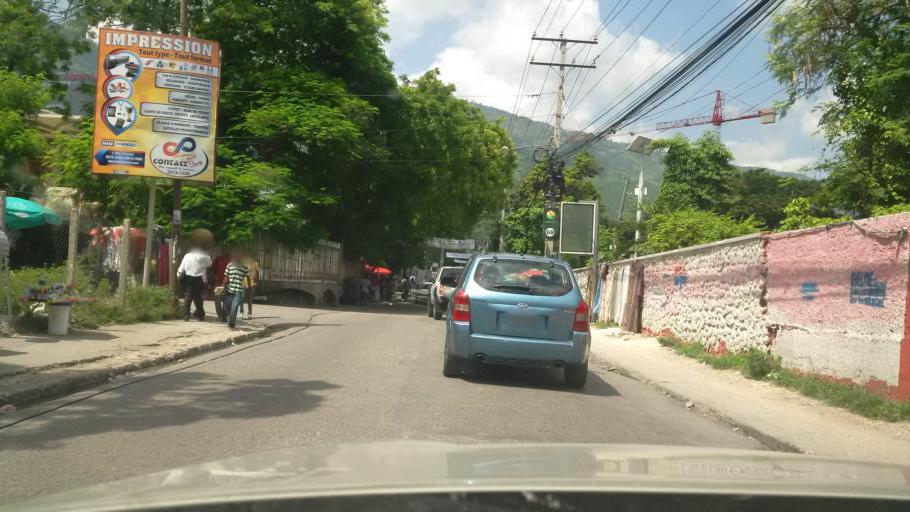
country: HT
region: Ouest
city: Port-au-Prince
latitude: 18.5354
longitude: -72.3239
